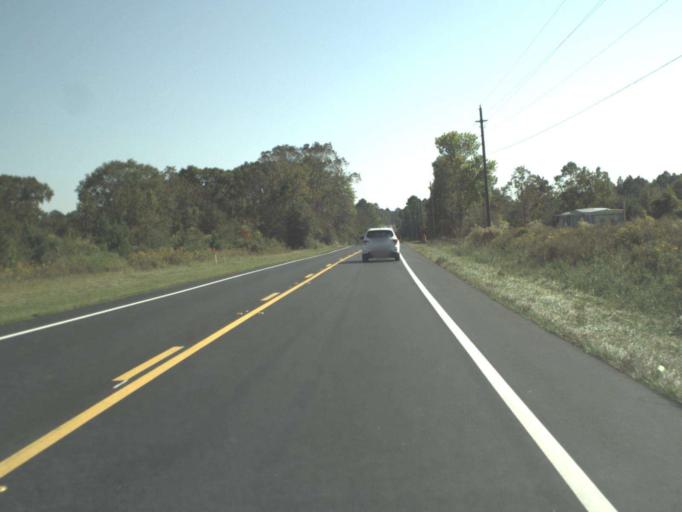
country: US
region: Alabama
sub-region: Covington County
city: Florala
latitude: 30.9427
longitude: -86.2833
